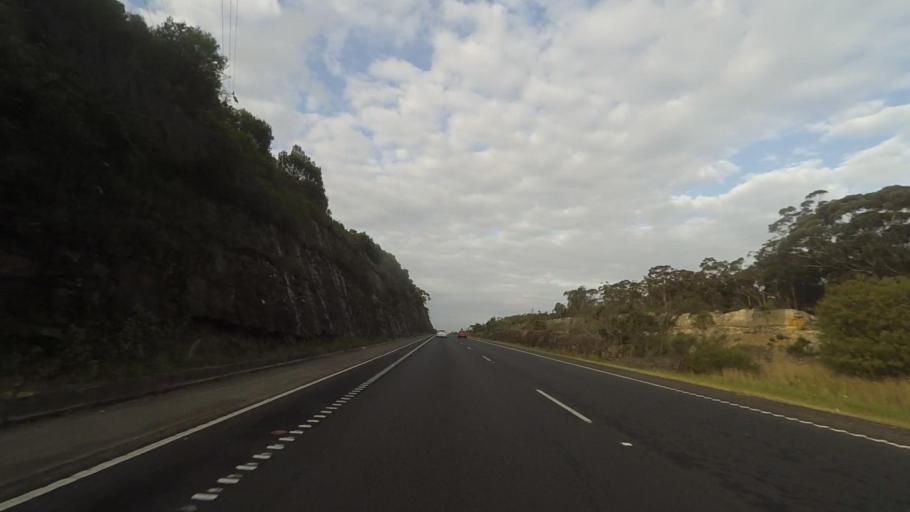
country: AU
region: New South Wales
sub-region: Wollongong
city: Helensburgh
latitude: -34.2238
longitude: 150.9507
